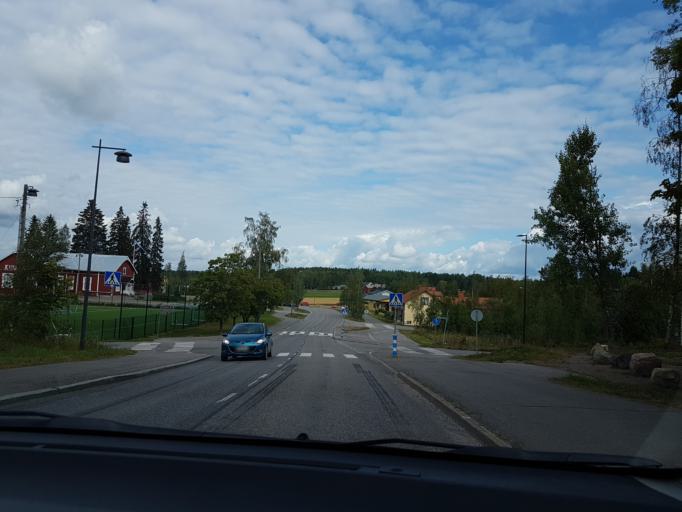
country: FI
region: Uusimaa
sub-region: Helsinki
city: Pornainen
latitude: 60.4785
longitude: 25.3743
